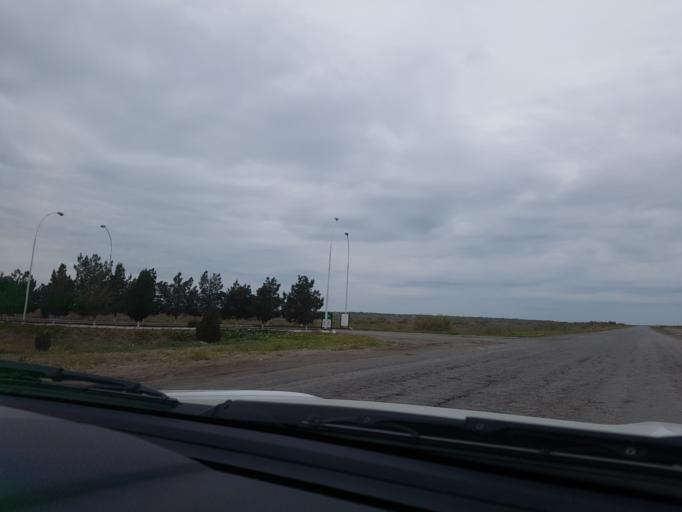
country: TM
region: Mary
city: Bayramaly
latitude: 37.9620
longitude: 62.6611
